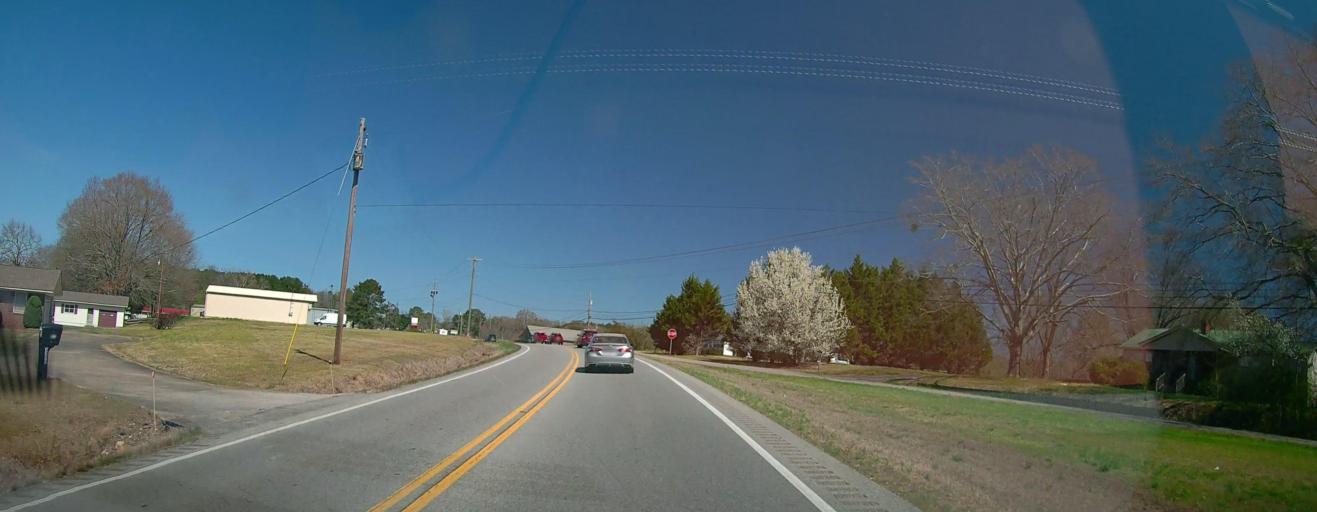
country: US
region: Alabama
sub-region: Etowah County
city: Southside
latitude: 33.9039
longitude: -86.0262
